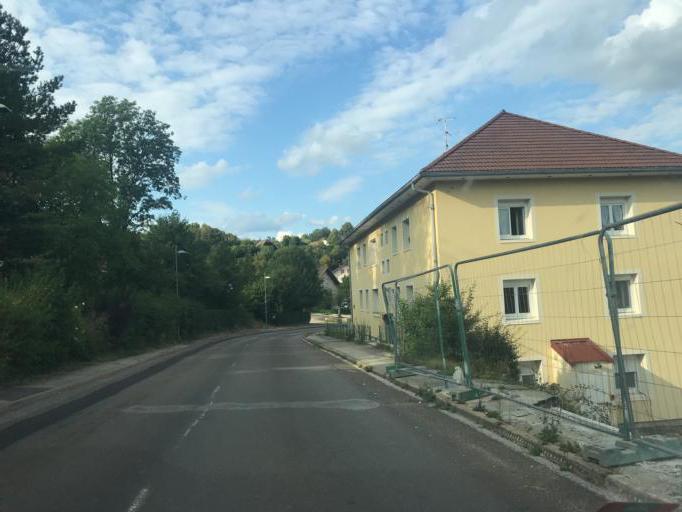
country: FR
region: Franche-Comte
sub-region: Departement du Jura
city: Lavans-les-Saint-Claude
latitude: 46.3876
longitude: 5.7867
